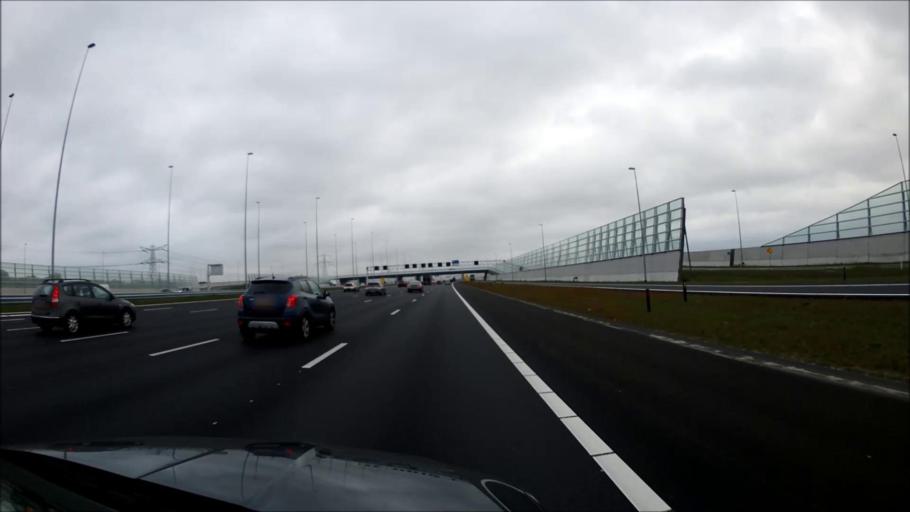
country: NL
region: North Holland
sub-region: Gemeente Weesp
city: Weesp
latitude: 52.3291
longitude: 5.0420
